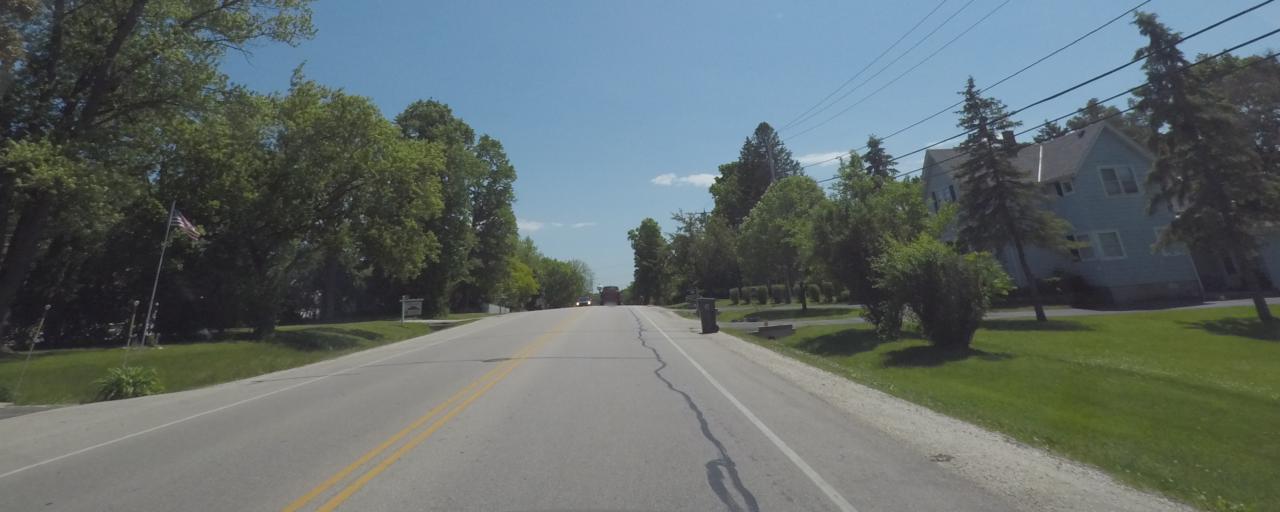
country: US
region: Wisconsin
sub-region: Waukesha County
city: New Berlin
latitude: 43.0143
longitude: -88.1271
